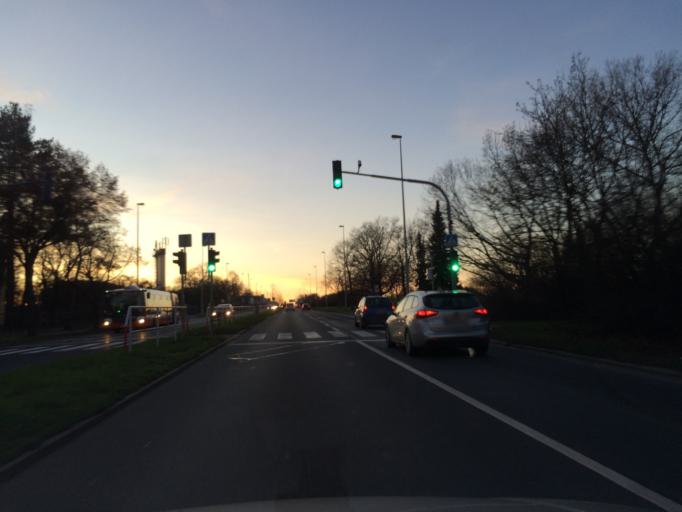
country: CZ
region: Central Bohemia
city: Horomerice
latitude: 50.0930
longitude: 14.3157
